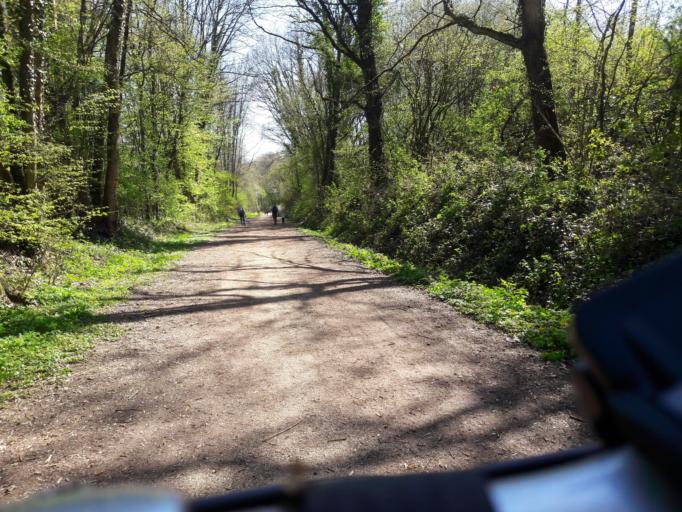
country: FR
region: Nord-Pas-de-Calais
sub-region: Departement du Nord
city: Ferriere-la-Grande
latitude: 50.2478
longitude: 4.0082
